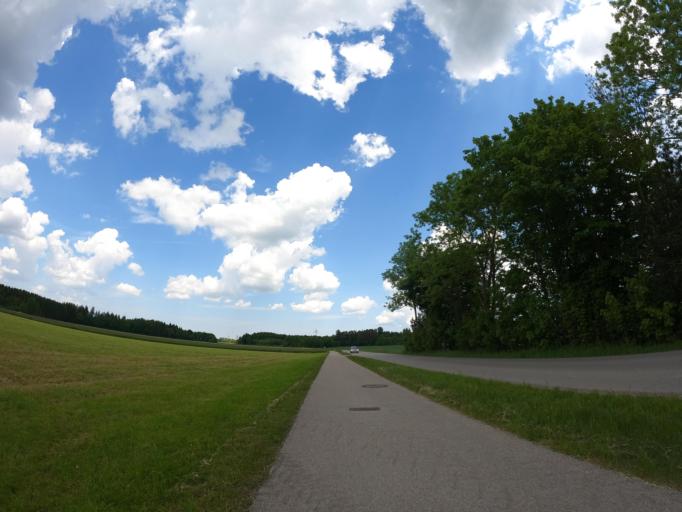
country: DE
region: Bavaria
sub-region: Upper Bavaria
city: Sauerlach
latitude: 47.9840
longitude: 11.6565
